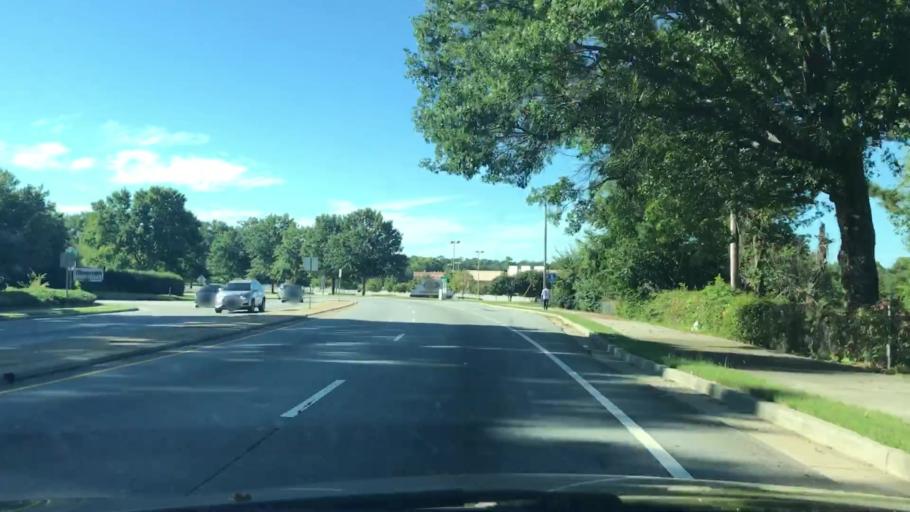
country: US
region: Georgia
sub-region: Gwinnett County
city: Mountain Park
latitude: 33.8216
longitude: -84.1210
